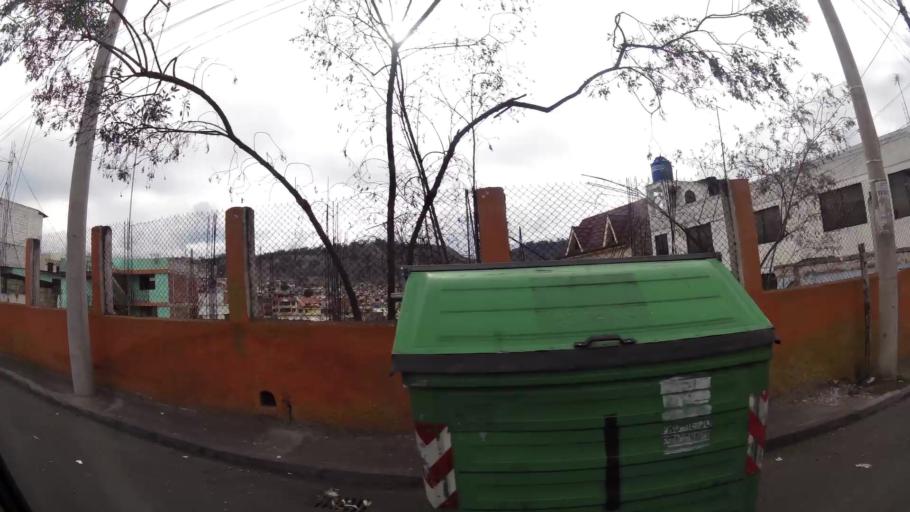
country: EC
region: Tungurahua
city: Ambato
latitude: -1.2585
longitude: -78.6288
